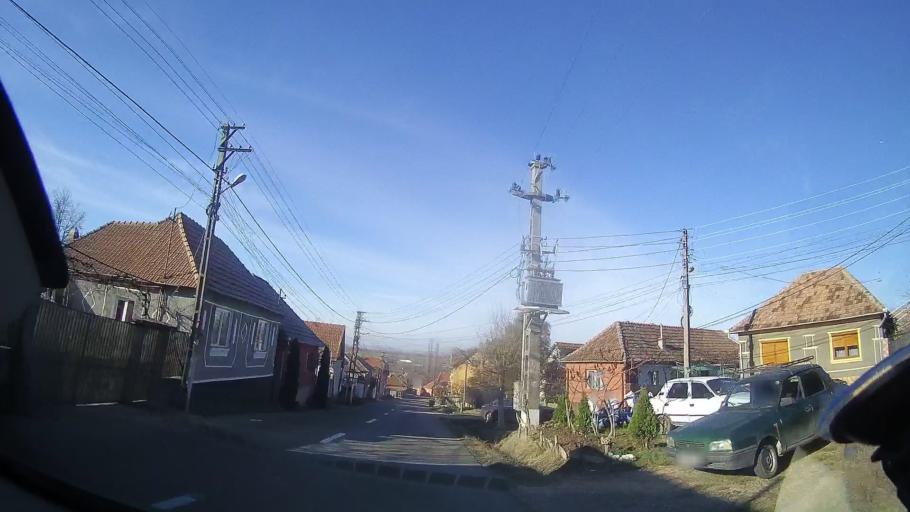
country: RO
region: Bihor
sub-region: Comuna Vadu Crisului
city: Vadu Crisului
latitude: 46.9896
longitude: 22.5247
